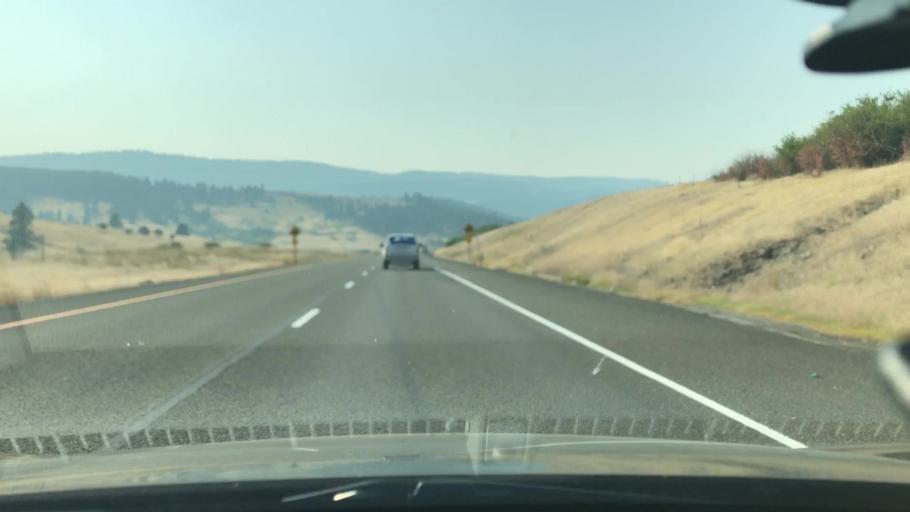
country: US
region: Oregon
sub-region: Union County
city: Union
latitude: 45.1912
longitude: -118.0005
